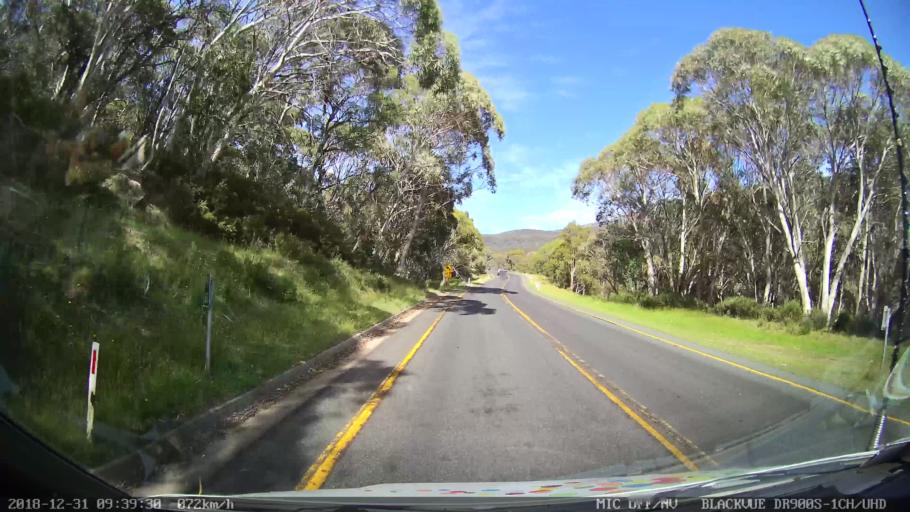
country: AU
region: New South Wales
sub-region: Snowy River
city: Jindabyne
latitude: -36.4793
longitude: 148.3541
